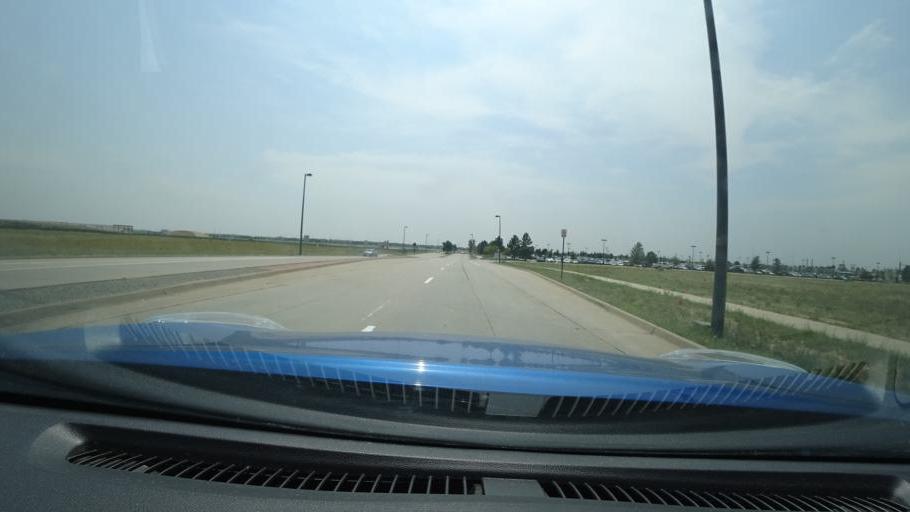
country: US
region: Colorado
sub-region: Adams County
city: Aurora
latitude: 39.7716
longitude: -104.7837
